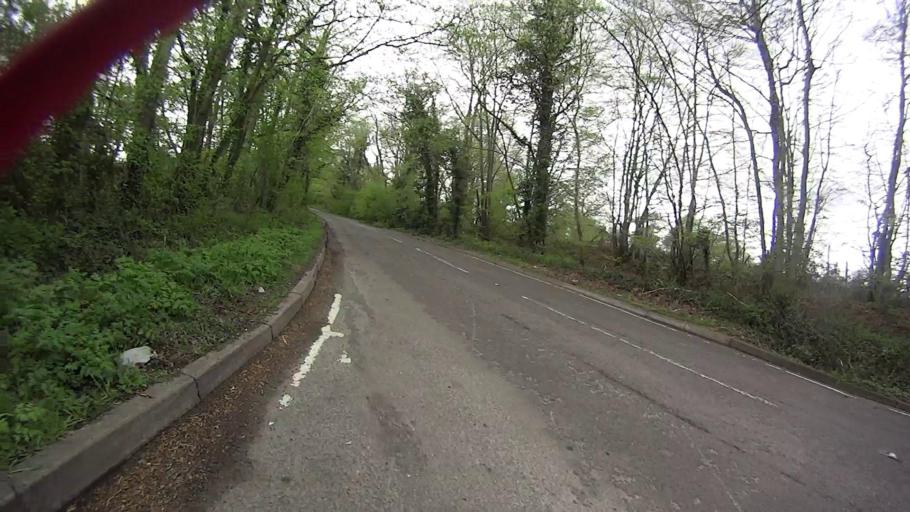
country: GB
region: England
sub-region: Surrey
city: Newdigate
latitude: 51.1335
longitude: -0.2755
